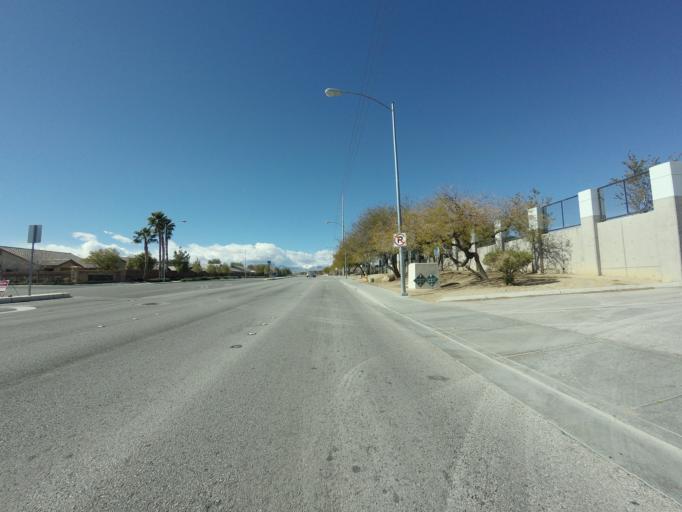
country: US
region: Nevada
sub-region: Clark County
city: Nellis Air Force Base
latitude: 36.2691
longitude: -115.1053
